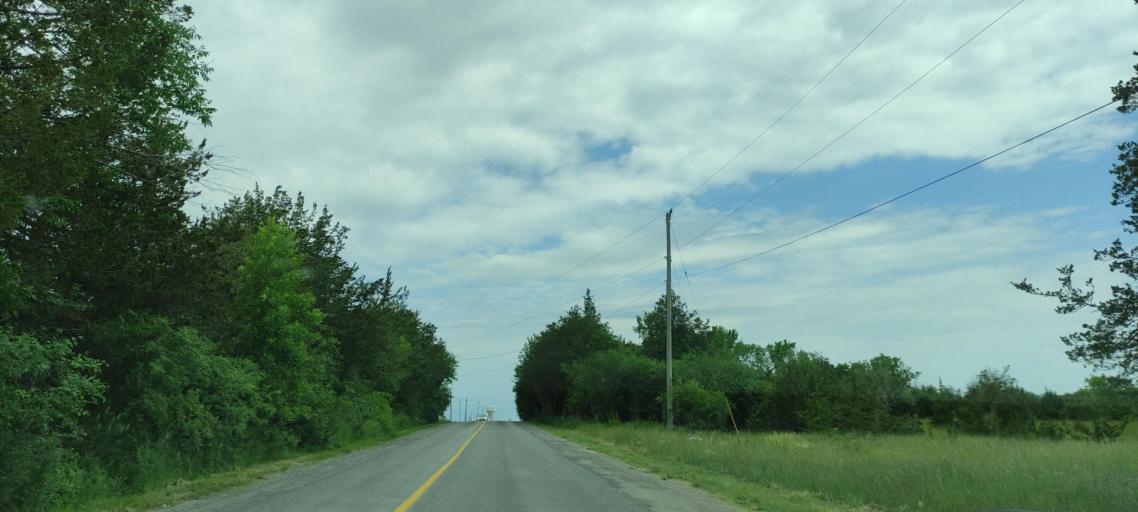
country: CA
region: Ontario
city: Quinte West
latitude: 44.0839
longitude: -77.5978
